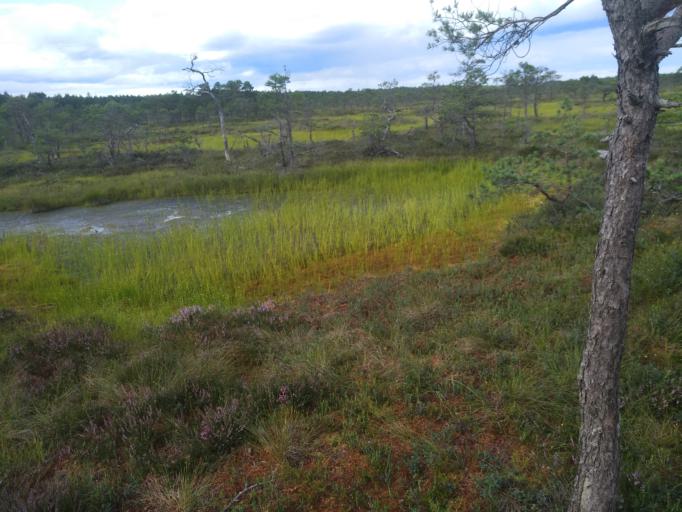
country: EE
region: Harju
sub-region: Anija vald
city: Kehra
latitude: 59.1887
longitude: 25.5187
